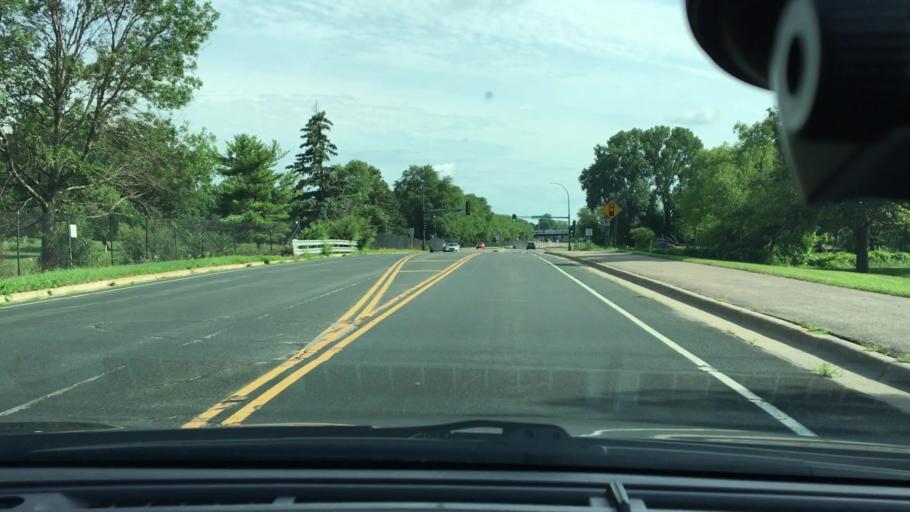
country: US
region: Minnesota
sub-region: Hennepin County
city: Golden Valley
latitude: 44.9800
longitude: -93.3905
